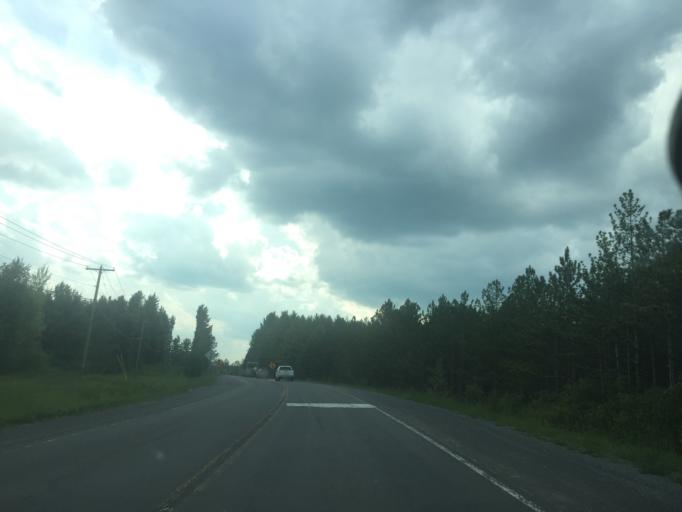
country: US
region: West Virginia
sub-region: Tucker County
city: Parsons
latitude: 39.1362
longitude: -79.4724
